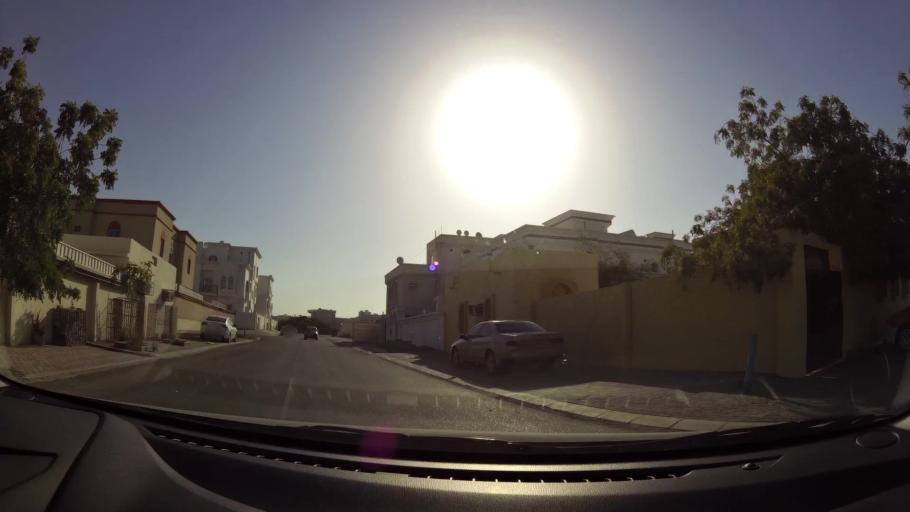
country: OM
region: Muhafazat Masqat
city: As Sib al Jadidah
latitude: 23.6220
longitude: 58.1873
